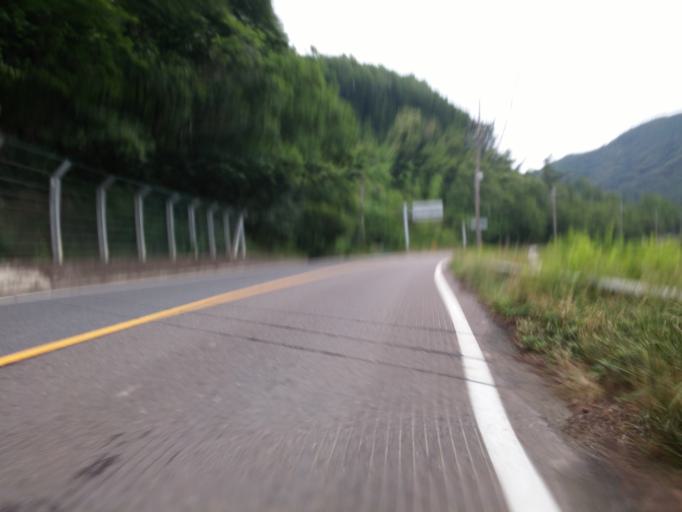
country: KR
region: Chungcheongbuk-do
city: Okcheon
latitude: 36.2502
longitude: 127.5122
